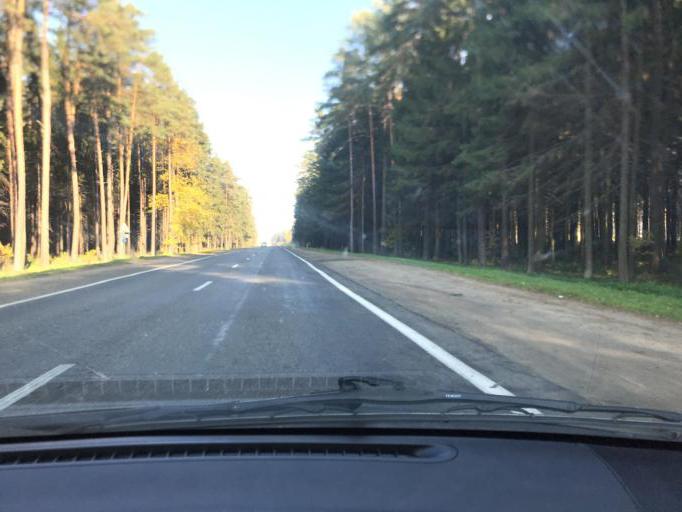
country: BY
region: Vitebsk
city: Orsha
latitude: 54.4101
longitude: 30.4553
